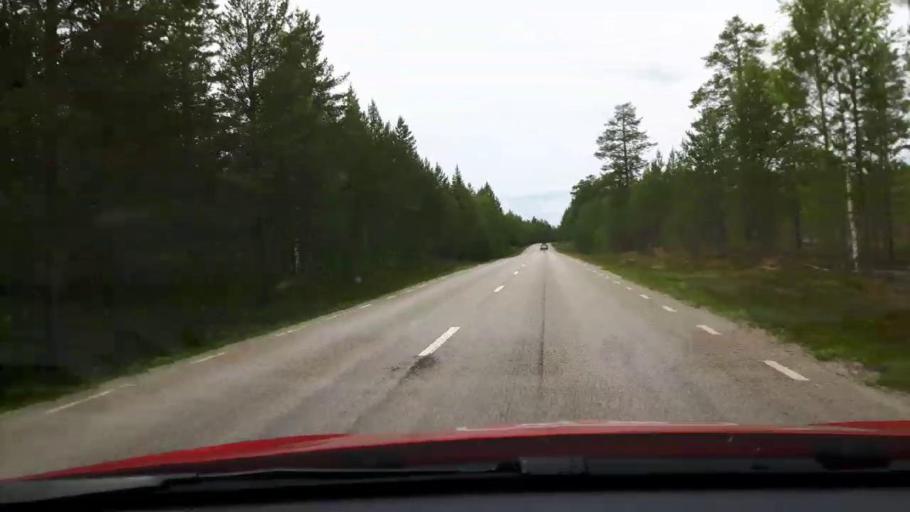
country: SE
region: Jaemtland
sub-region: Harjedalens Kommun
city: Sveg
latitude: 62.2413
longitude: 13.8477
